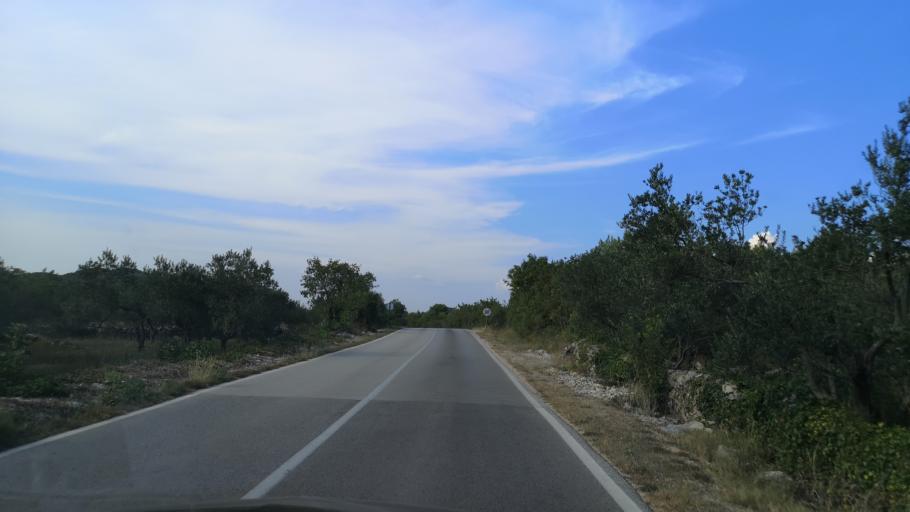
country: HR
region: Sibensko-Kniniska
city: Vodice
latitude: 43.7900
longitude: 15.7708
